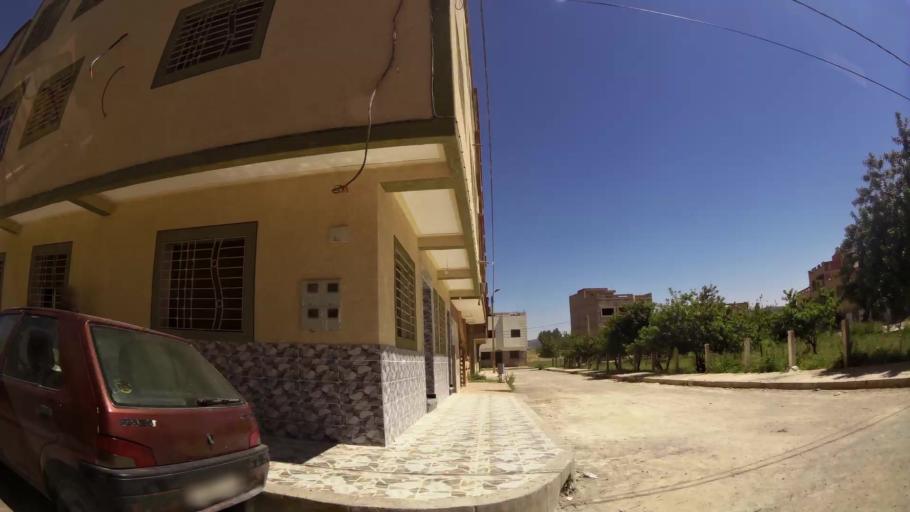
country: MA
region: Oriental
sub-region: Oujda-Angad
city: Oujda
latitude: 34.6696
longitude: -1.8681
